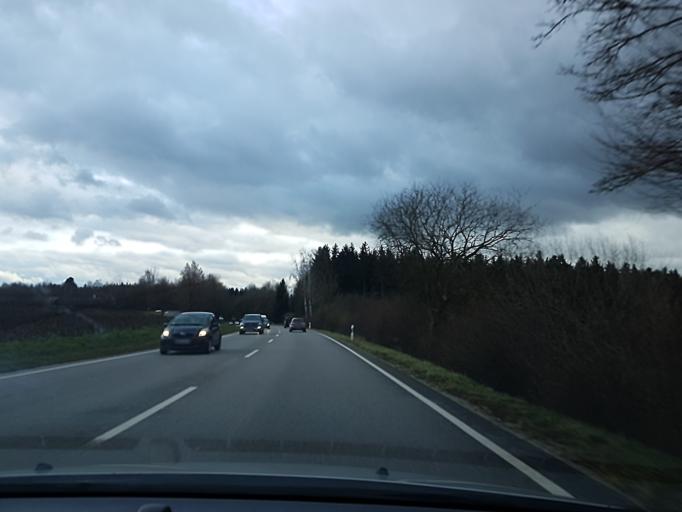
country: DE
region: Bavaria
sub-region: Lower Bavaria
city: Kumhausen
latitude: 48.5073
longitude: 12.2083
